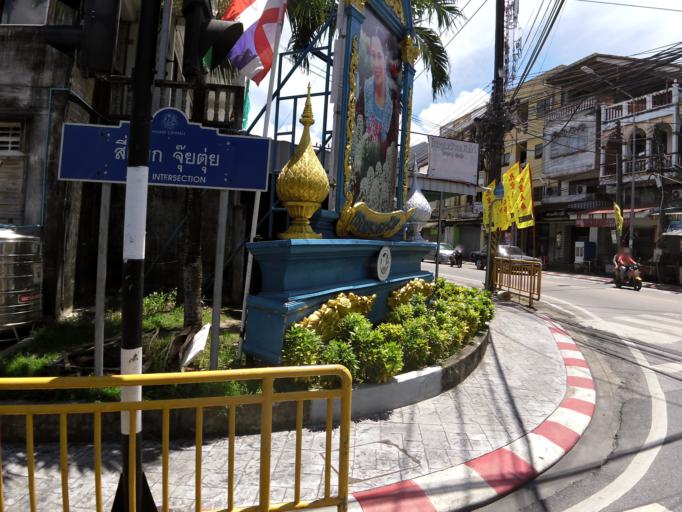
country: TH
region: Phuket
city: Ban Talat Nua
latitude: 7.8837
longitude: 98.3827
